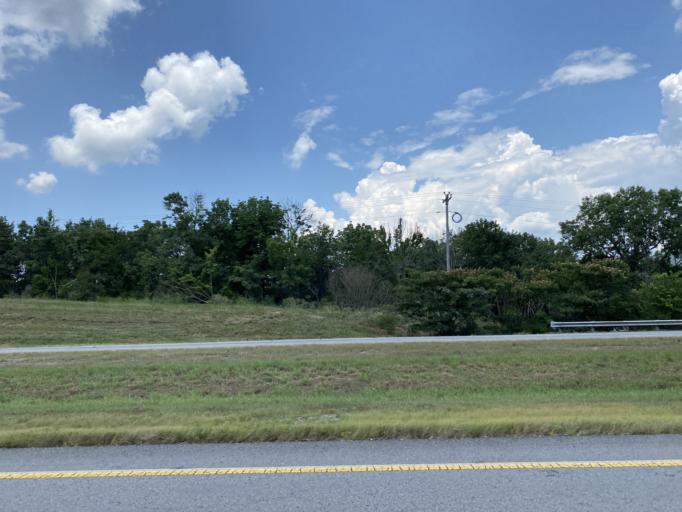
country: US
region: Alabama
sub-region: Jackson County
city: Scottsboro
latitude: 34.6166
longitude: -86.1157
